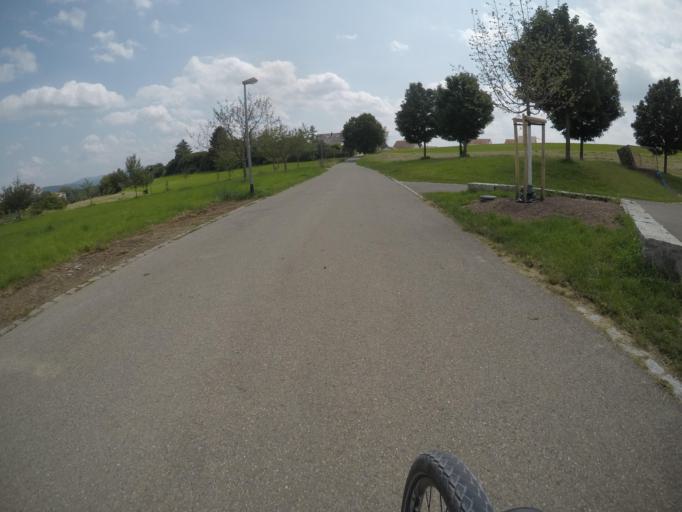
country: DE
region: Baden-Wuerttemberg
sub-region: Freiburg Region
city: Zimmern ob Rottweil
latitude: 48.1736
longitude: 8.6055
